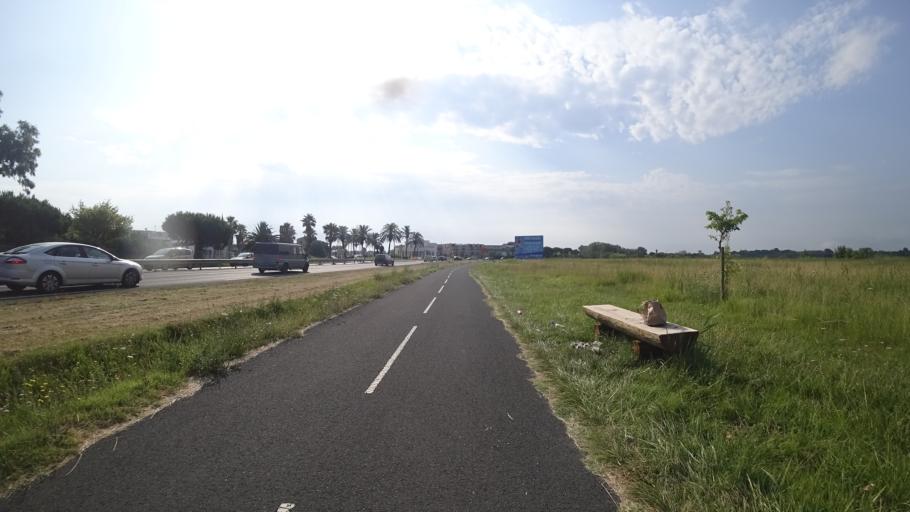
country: FR
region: Languedoc-Roussillon
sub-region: Departement des Pyrenees-Orientales
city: Canet-en-Roussillon
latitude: 42.6988
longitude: 3.0216
